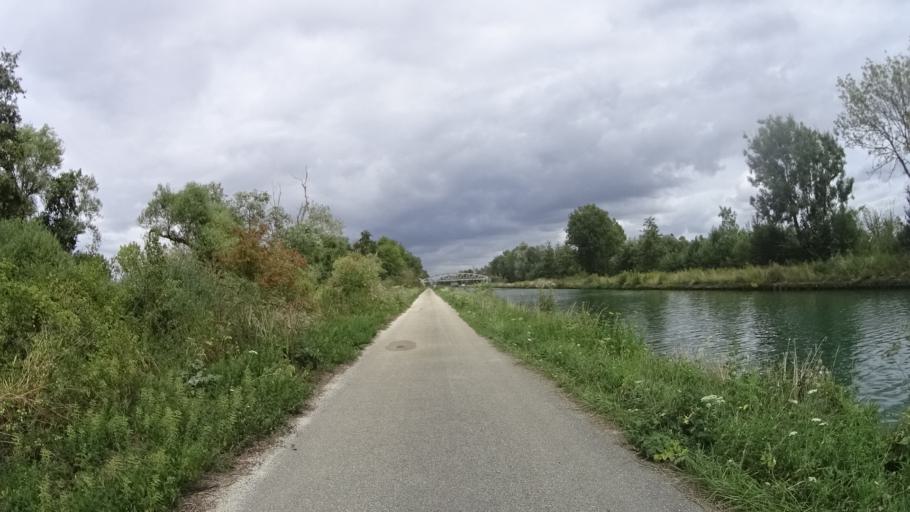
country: FR
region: Picardie
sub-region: Departement de l'Aisne
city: Viry-Noureuil
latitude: 49.6214
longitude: 3.2499
